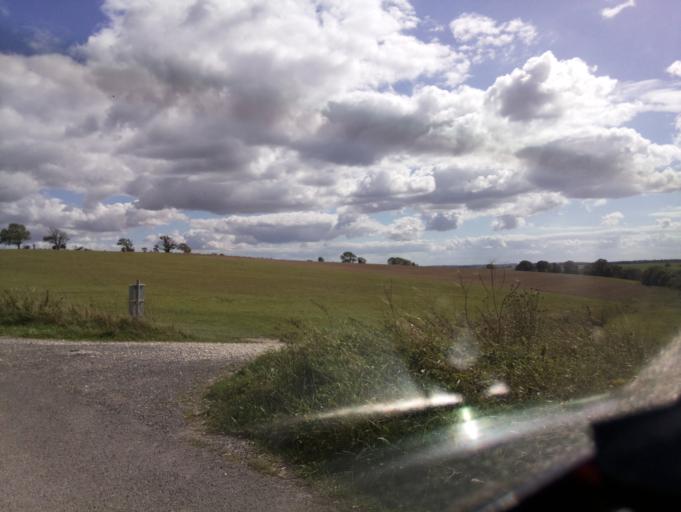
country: GB
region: England
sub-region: Wiltshire
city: Erlestoke
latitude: 51.2754
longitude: -2.0716
